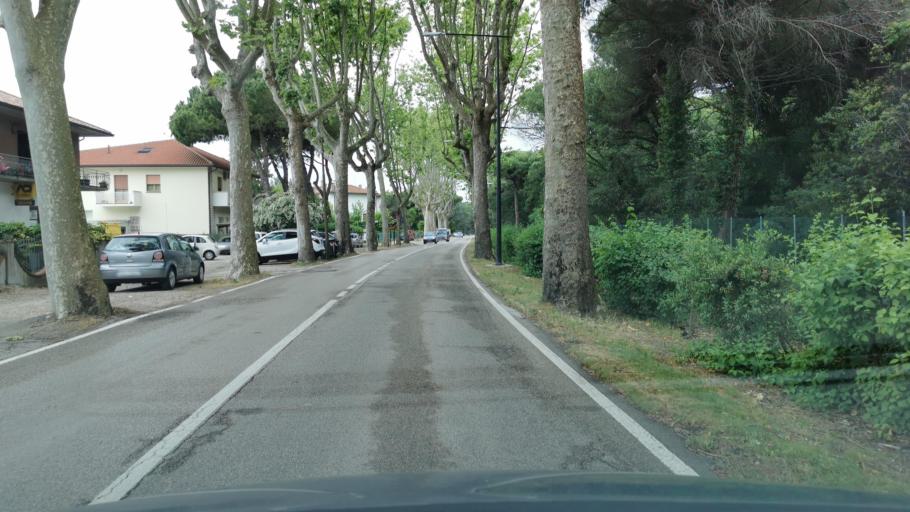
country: IT
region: Emilia-Romagna
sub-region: Provincia di Ravenna
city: Cervia
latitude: 44.2665
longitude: 12.3355
